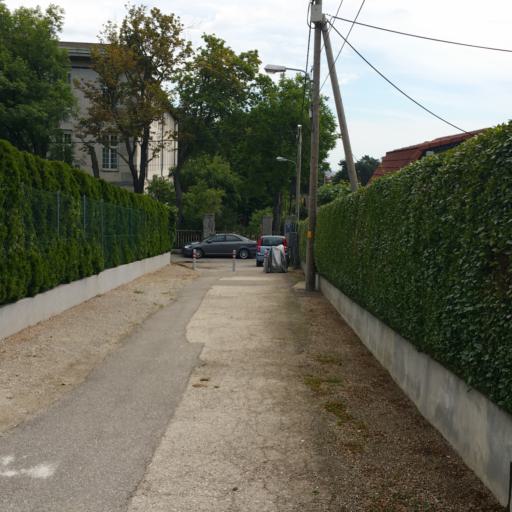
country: AT
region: Vienna
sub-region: Wien Stadt
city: Vienna
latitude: 48.2095
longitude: 16.2956
